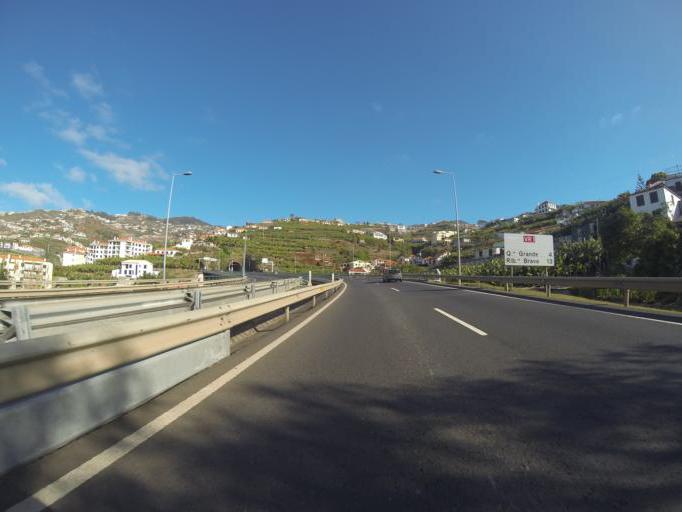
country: PT
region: Madeira
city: Camara de Lobos
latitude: 32.6596
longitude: -16.9757
